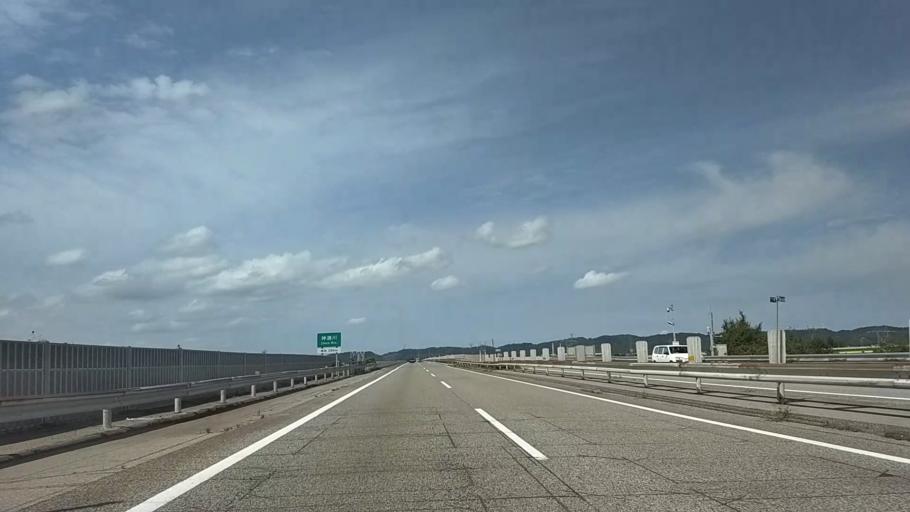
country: JP
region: Toyama
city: Toyama-shi
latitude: 36.6619
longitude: 137.1940
